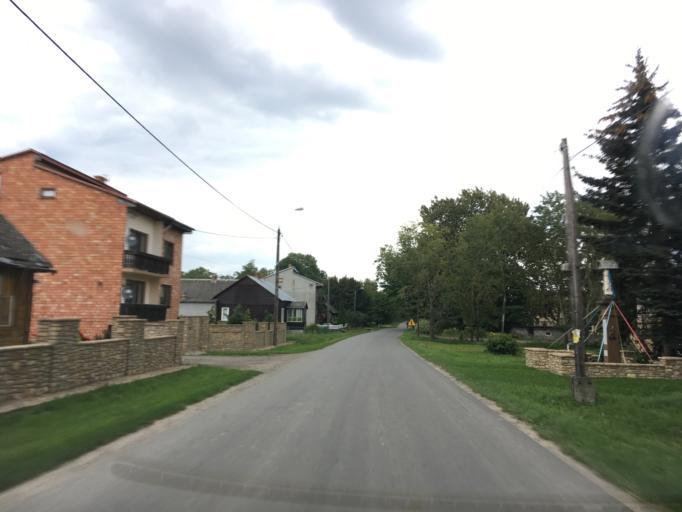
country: PL
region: Lesser Poland Voivodeship
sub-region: Powiat olkuski
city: Wolbrom
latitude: 50.4795
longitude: 19.8220
